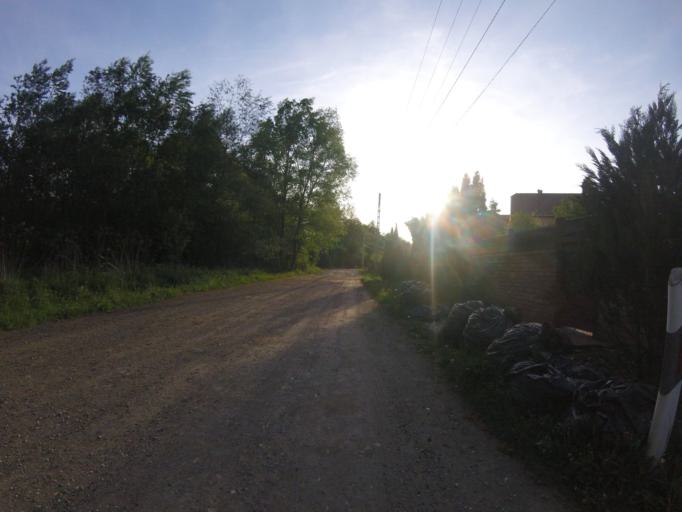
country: HU
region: Pest
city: Pilisszentivan
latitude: 47.6133
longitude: 18.8807
